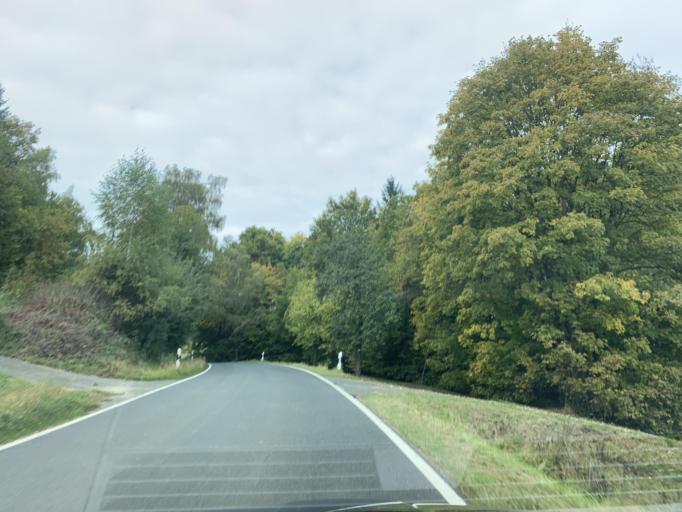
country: DE
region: Bavaria
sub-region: Upper Franconia
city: Gossweinstein
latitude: 49.7860
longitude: 11.3144
